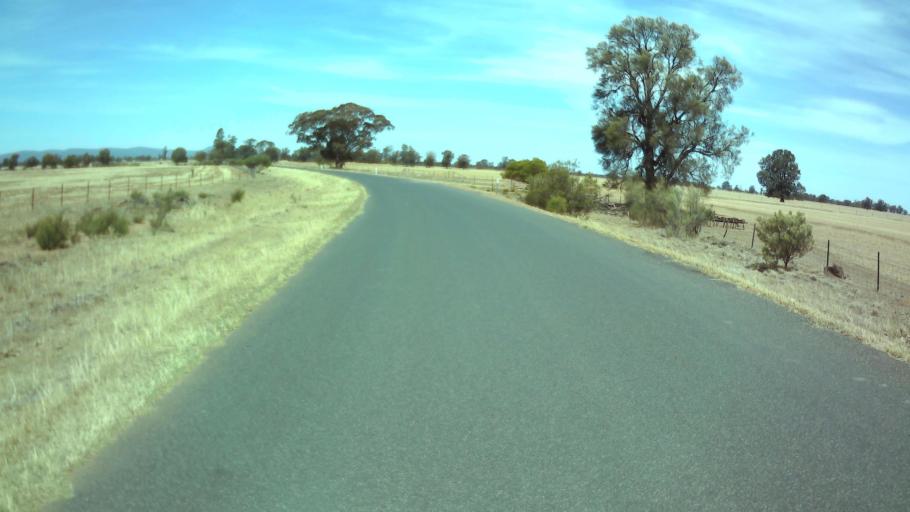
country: AU
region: New South Wales
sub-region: Weddin
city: Grenfell
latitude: -33.9399
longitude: 147.7639
